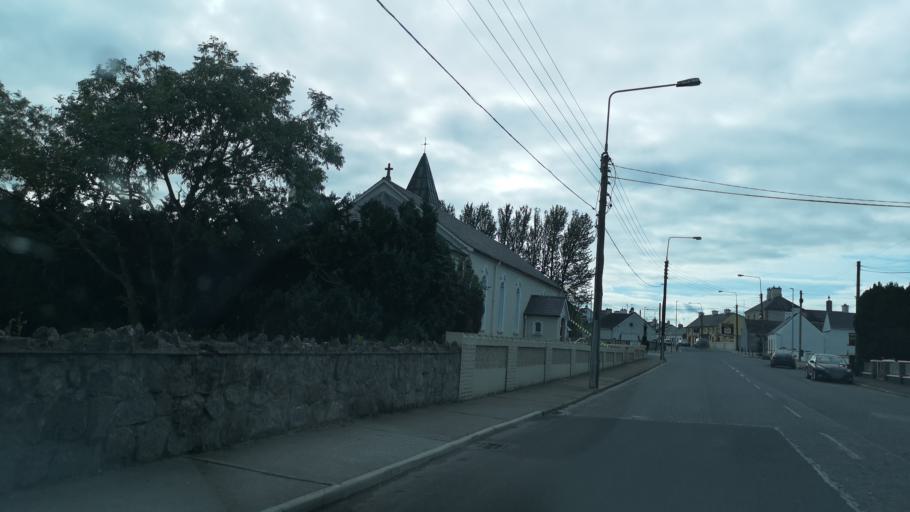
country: IE
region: Leinster
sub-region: Uibh Fhaili
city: Banagher
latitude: 53.2793
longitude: -8.0423
